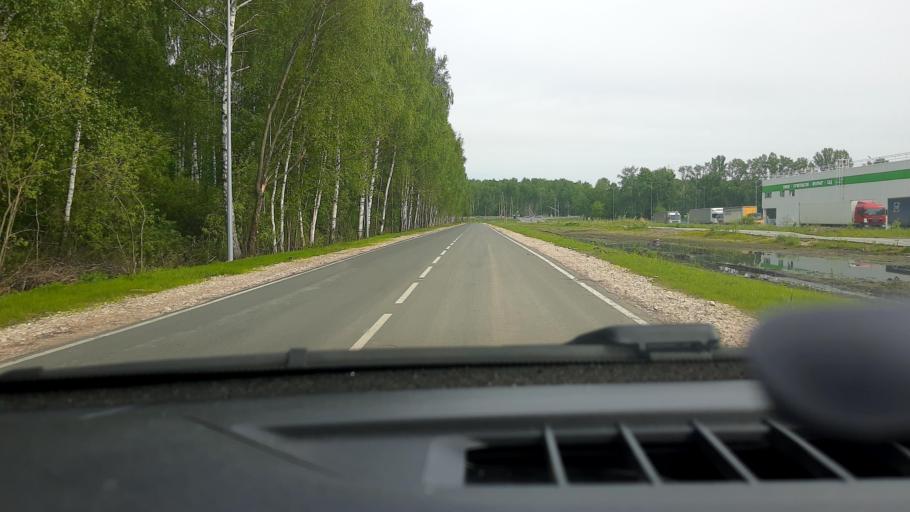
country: RU
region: Nizjnij Novgorod
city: Gorbatovka
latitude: 56.3062
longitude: 43.7695
